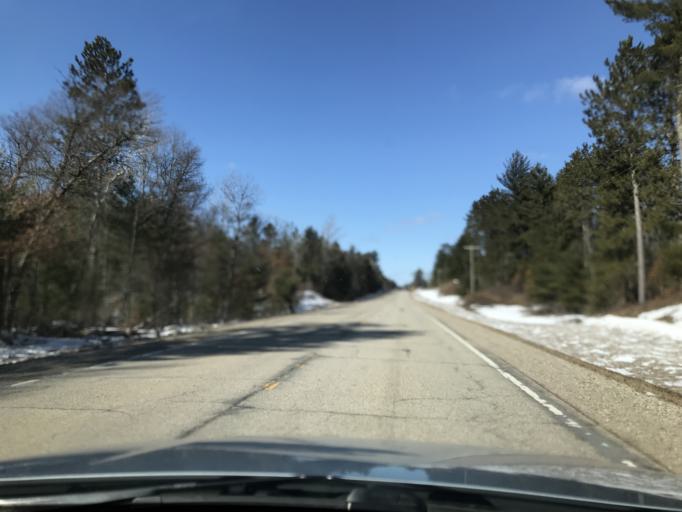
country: US
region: Wisconsin
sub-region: Marinette County
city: Niagara
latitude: 45.3949
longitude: -88.0994
